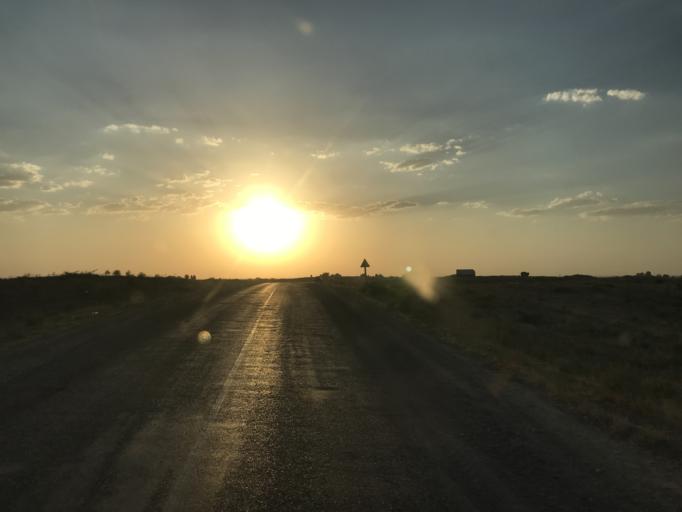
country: UZ
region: Toshkent
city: Yangiyul
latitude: 41.3373
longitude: 68.8817
